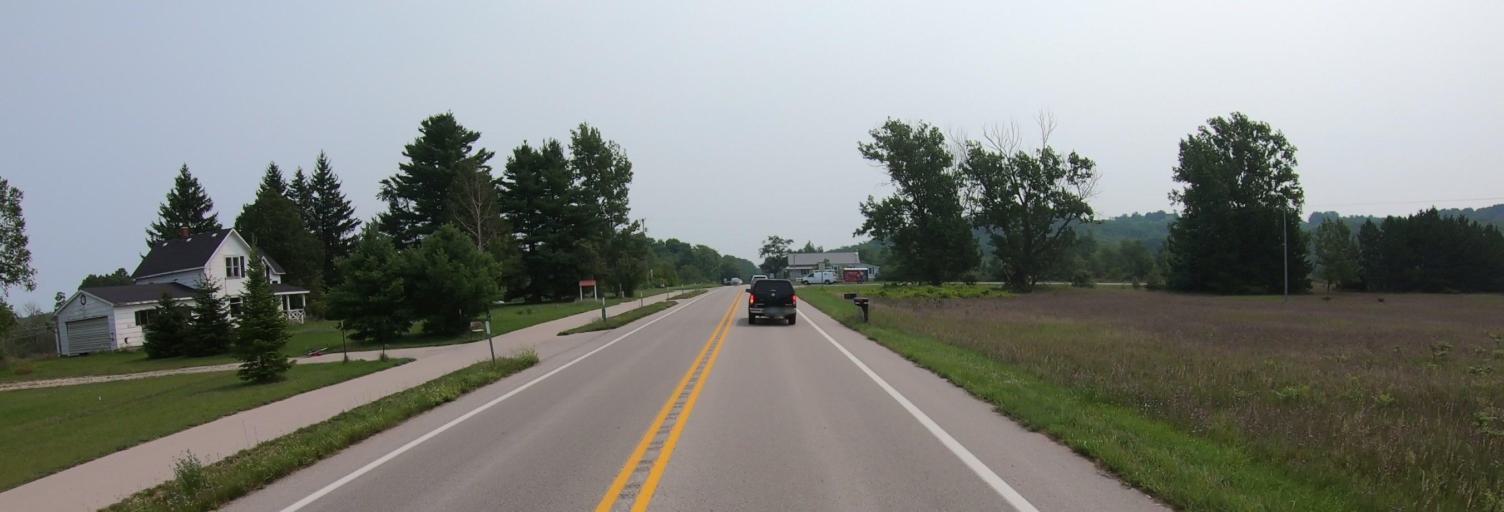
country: US
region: Michigan
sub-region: Leelanau County
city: Leland
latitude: 44.9219
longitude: -85.8742
